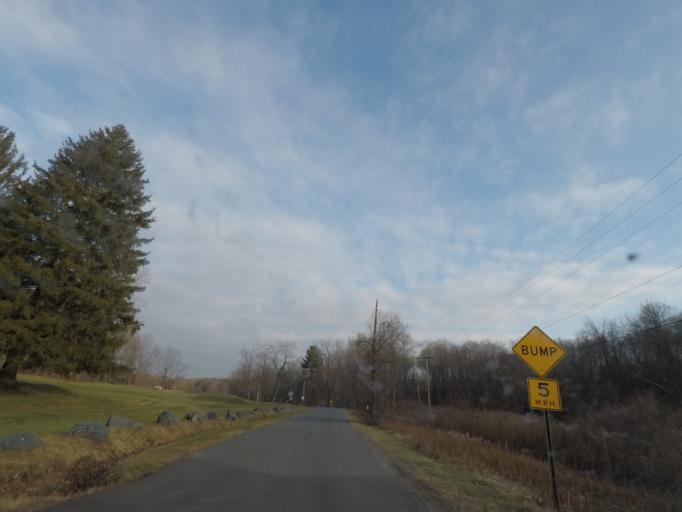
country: US
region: New York
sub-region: Rensselaer County
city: Wynantskill
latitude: 42.7213
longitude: -73.6385
